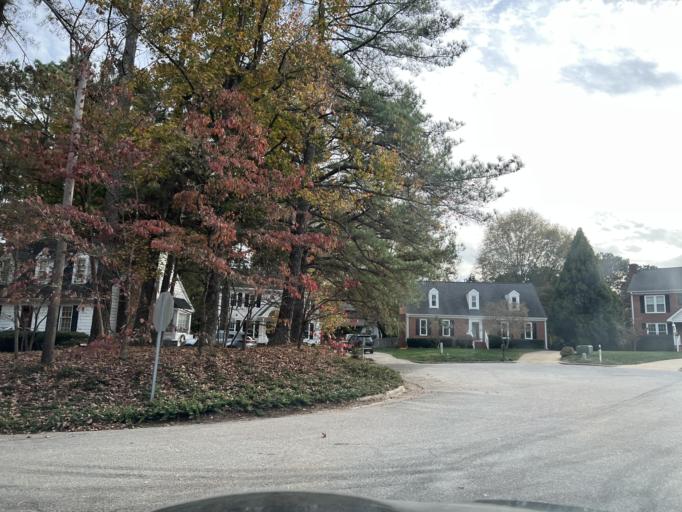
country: US
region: North Carolina
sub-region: Wake County
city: Wake Forest
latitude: 35.8959
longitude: -78.5968
